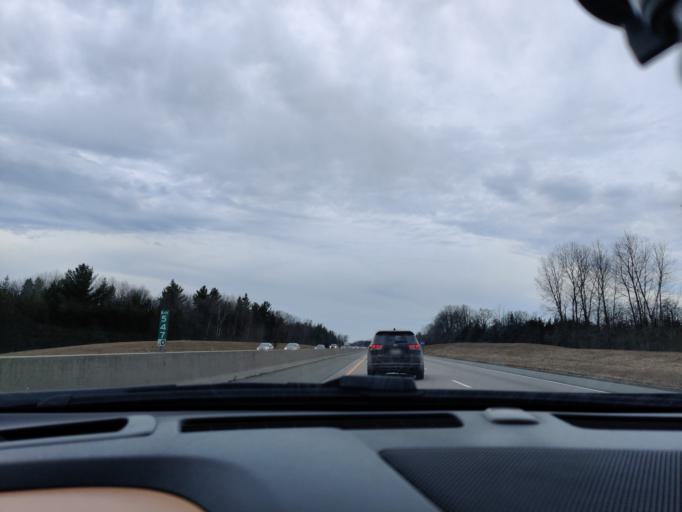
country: CA
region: Ontario
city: Belleville
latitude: 44.2082
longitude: -77.3483
